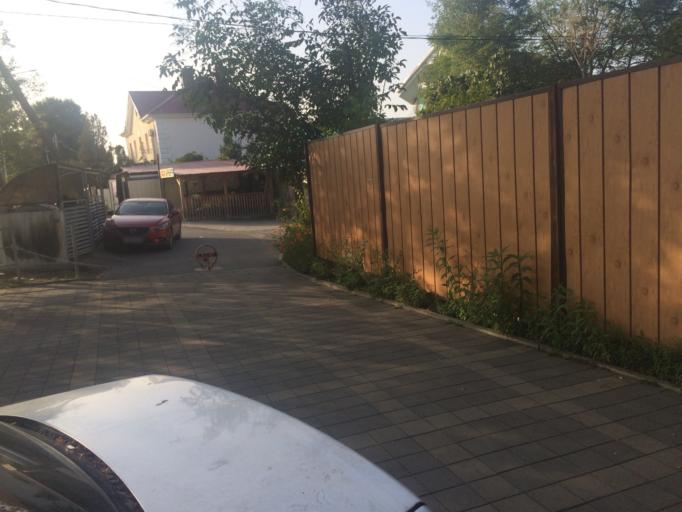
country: RU
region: Krasnodarskiy
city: Adler
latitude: 43.3870
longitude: 39.9891
